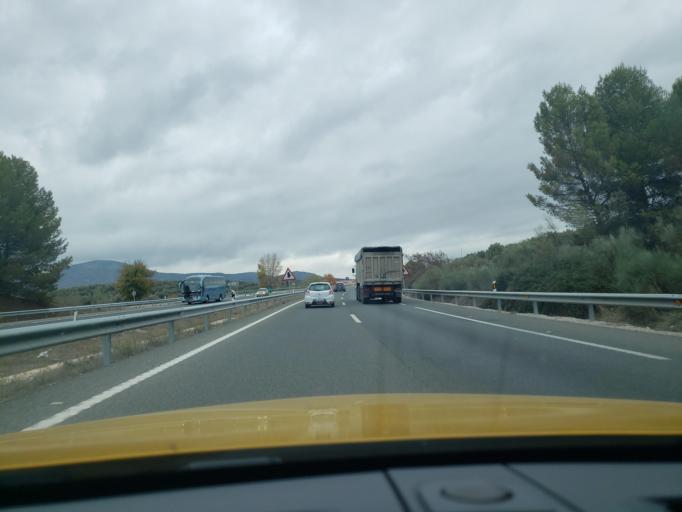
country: ES
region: Andalusia
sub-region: Provincia de Granada
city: Deifontes
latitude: 37.3655
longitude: -3.6051
